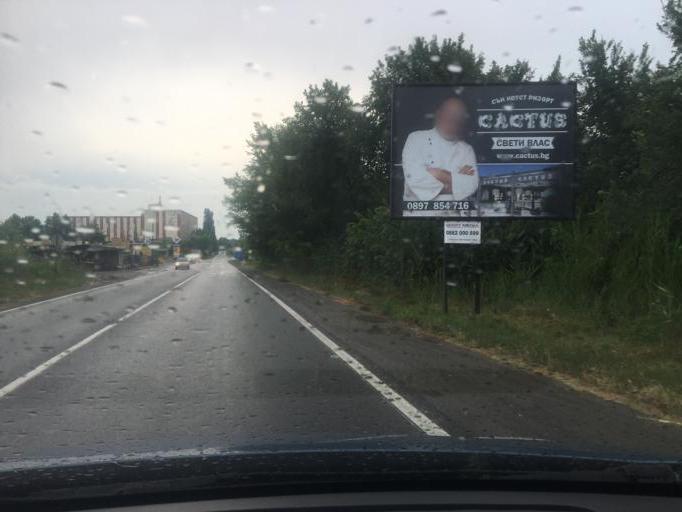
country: BG
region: Burgas
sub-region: Obshtina Pomorie
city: Pomorie
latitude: 42.5770
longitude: 27.6071
